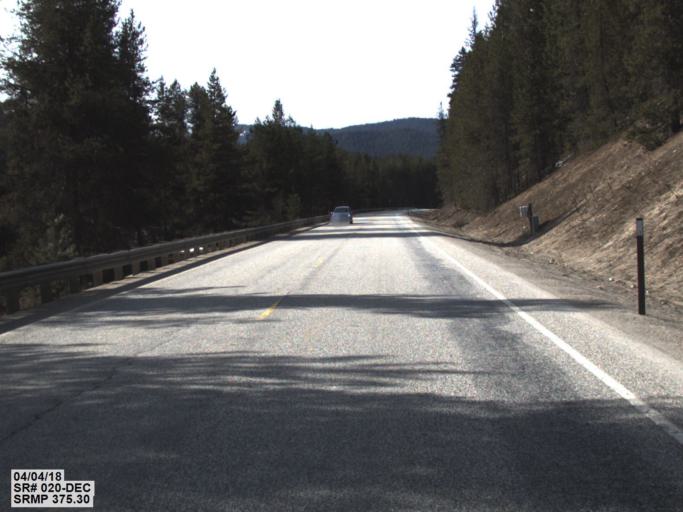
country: US
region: Washington
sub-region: Stevens County
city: Chewelah
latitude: 48.5597
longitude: -117.5569
